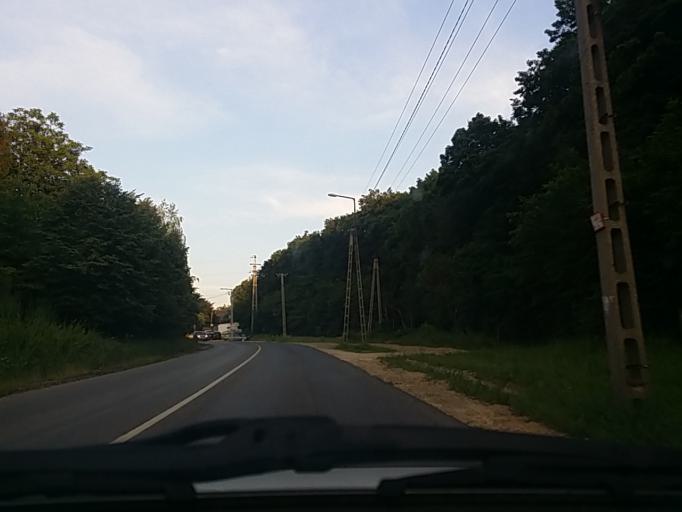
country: HU
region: Pest
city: Solymar
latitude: 47.5703
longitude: 18.9464
